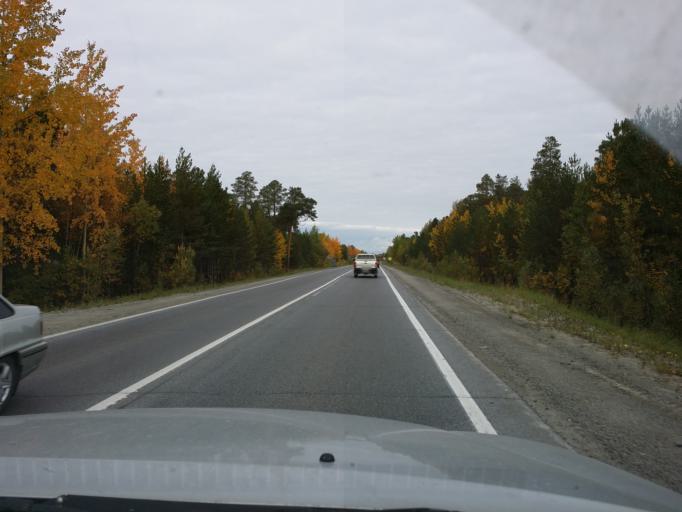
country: RU
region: Khanty-Mansiyskiy Avtonomnyy Okrug
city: Megion
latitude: 61.1025
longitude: 75.8554
